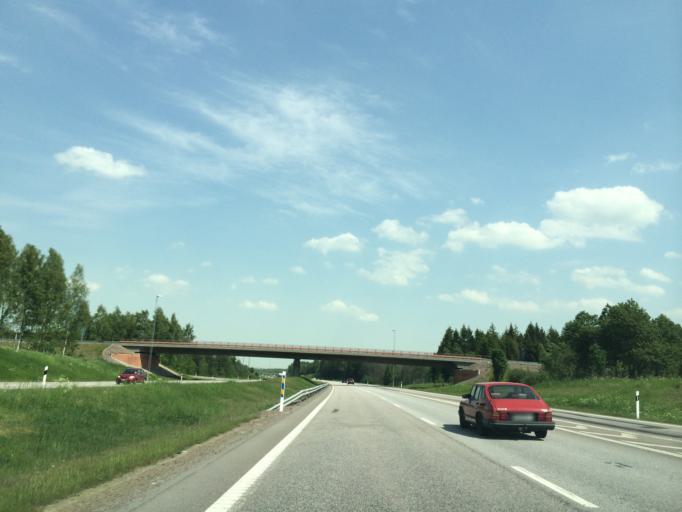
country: SE
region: OEstergoetland
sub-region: Vadstena Kommun
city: Herrestad
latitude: 58.2946
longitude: 14.9214
